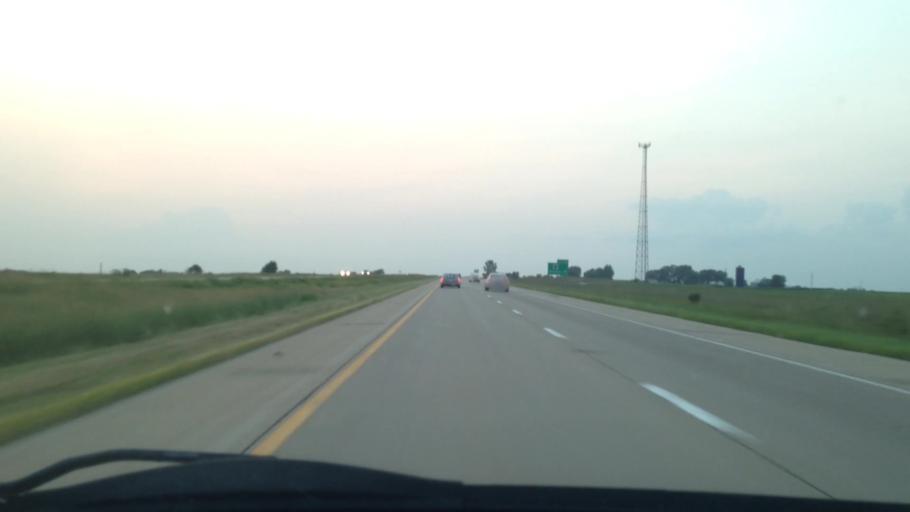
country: US
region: Iowa
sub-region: Benton County
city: Urbana
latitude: 42.3065
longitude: -91.9706
